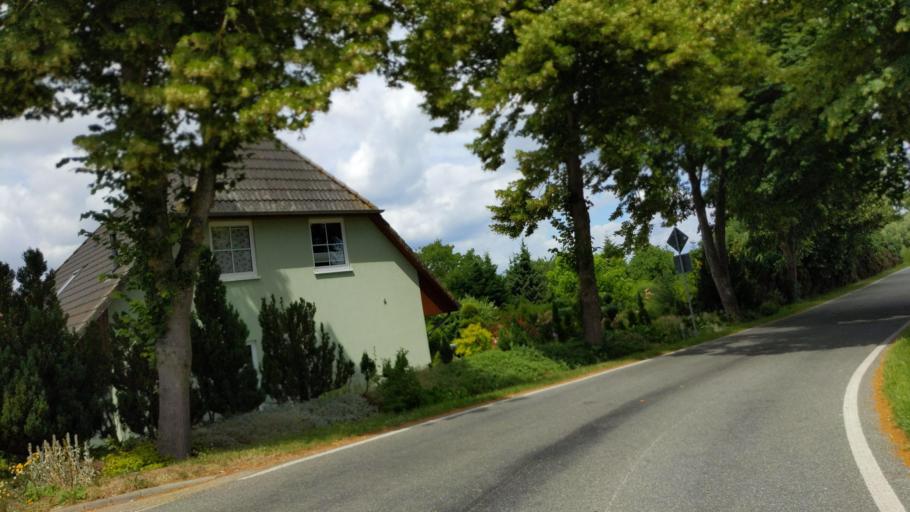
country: DE
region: Mecklenburg-Vorpommern
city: Dassow
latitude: 53.9332
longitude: 10.9684
